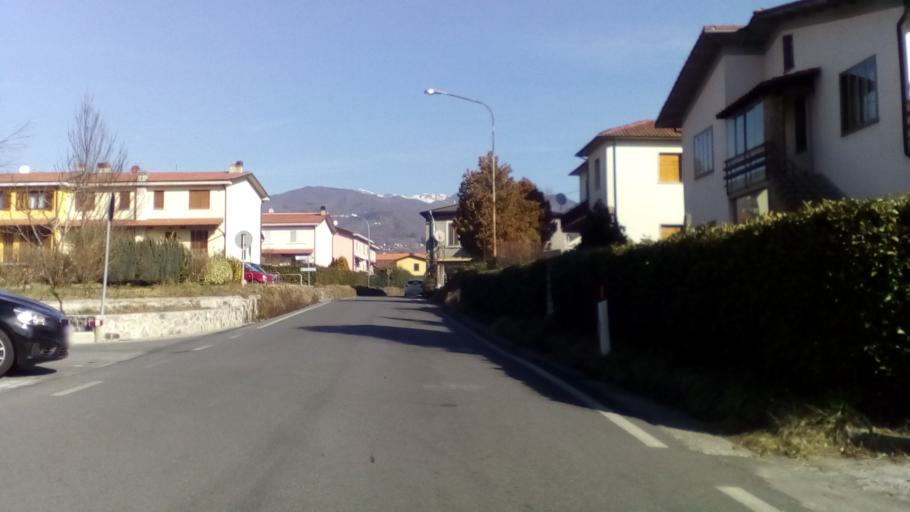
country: IT
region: Tuscany
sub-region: Provincia di Lucca
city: Pieve Fosciana
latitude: 44.1223
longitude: 10.4094
